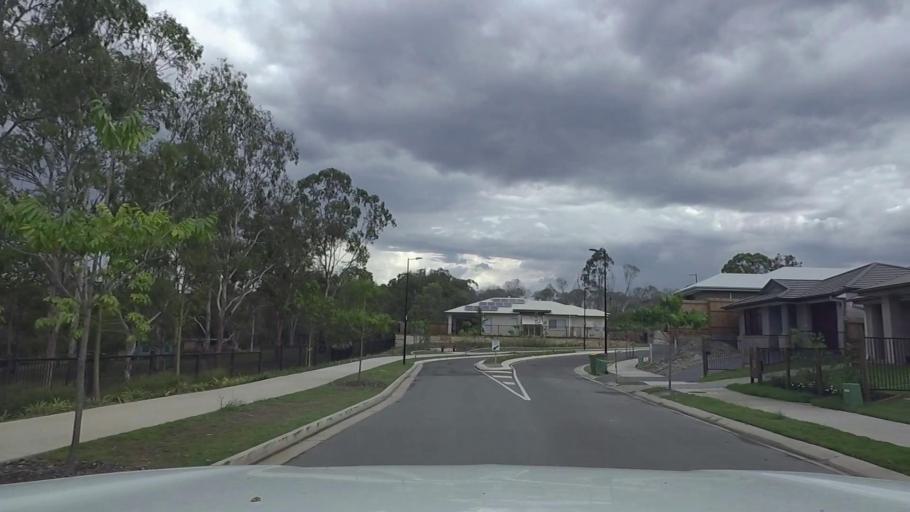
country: AU
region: Queensland
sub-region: Logan
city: Windaroo
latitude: -27.7329
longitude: 153.1669
